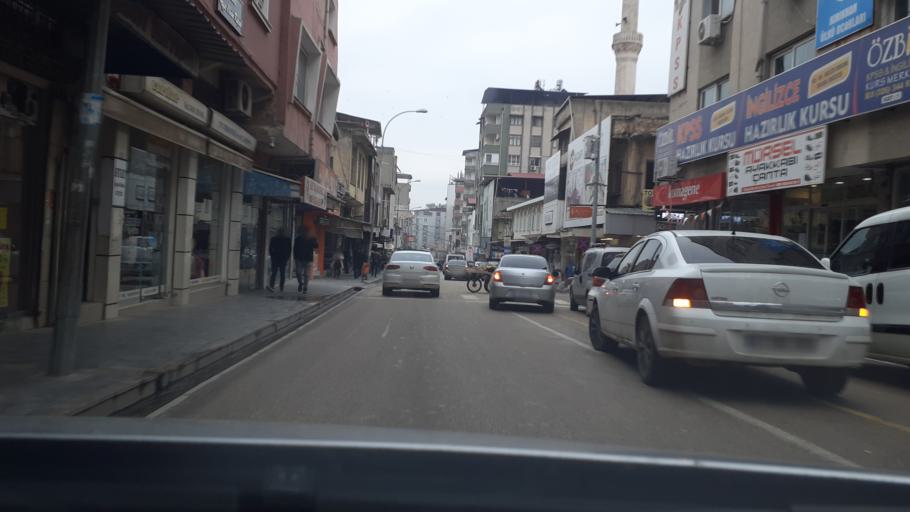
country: TR
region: Hatay
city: Kirikhan
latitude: 36.4989
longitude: 36.3550
